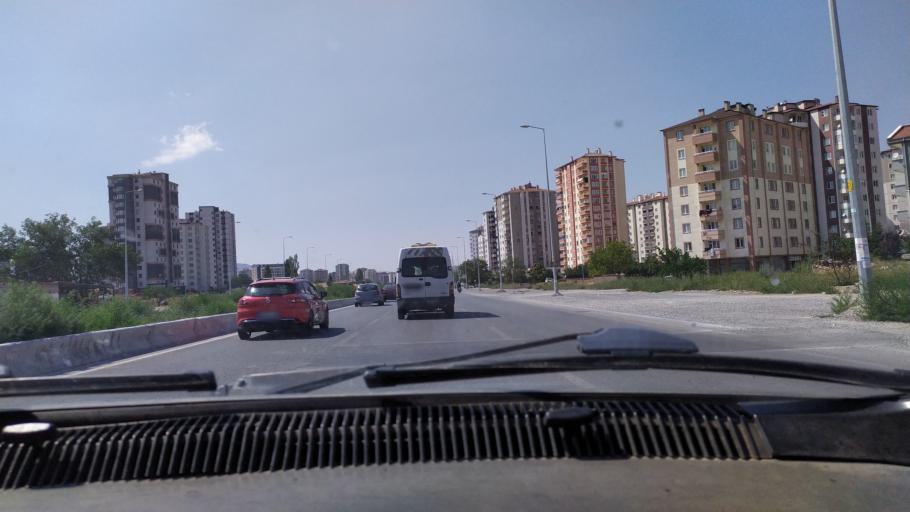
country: TR
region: Kayseri
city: Talas
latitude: 38.7214
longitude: 35.5364
